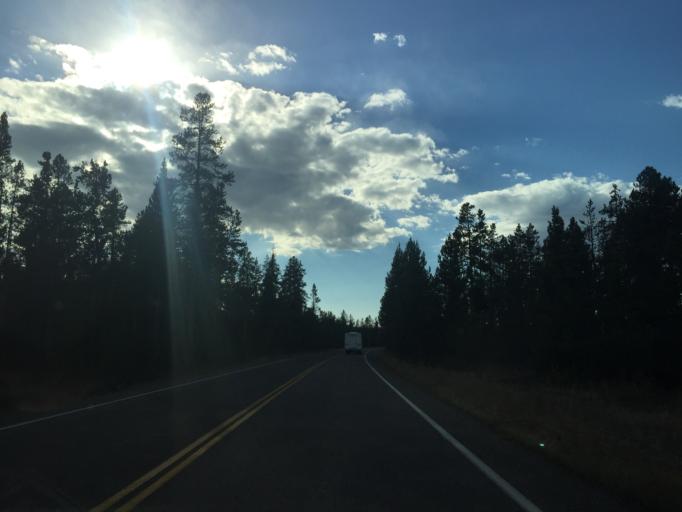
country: US
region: Montana
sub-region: Gallatin County
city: West Yellowstone
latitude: 44.6516
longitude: -111.0537
